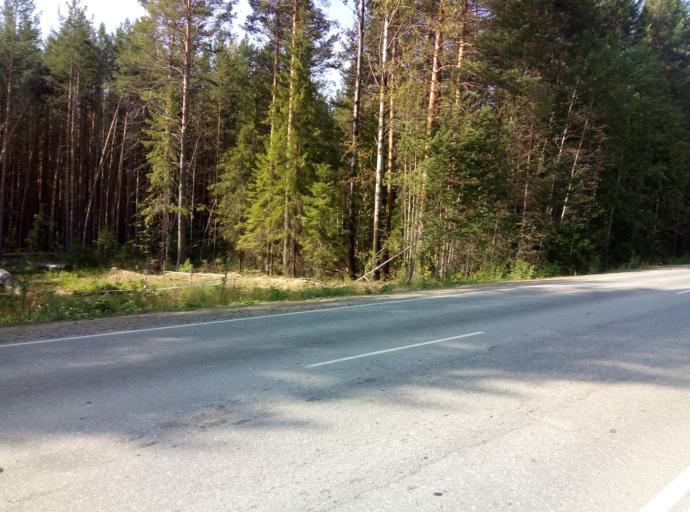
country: RU
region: Sverdlovsk
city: Krasnotur'insk
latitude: 59.7265
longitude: 60.2099
